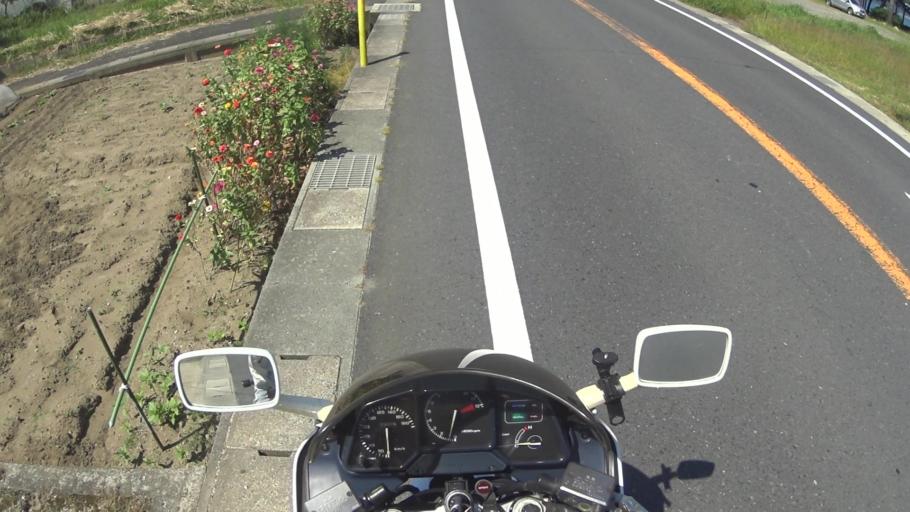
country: JP
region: Kyoto
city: Miyazu
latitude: 35.5225
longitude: 135.2742
